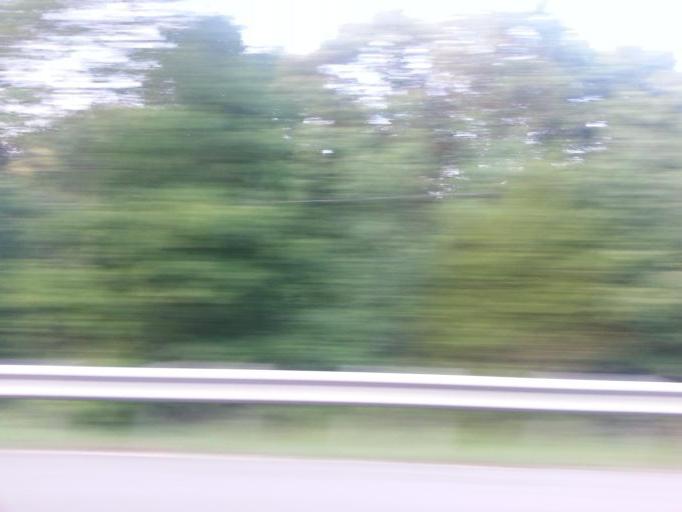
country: US
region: Tennessee
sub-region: Loudon County
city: Loudon
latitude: 35.7810
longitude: -84.3413
